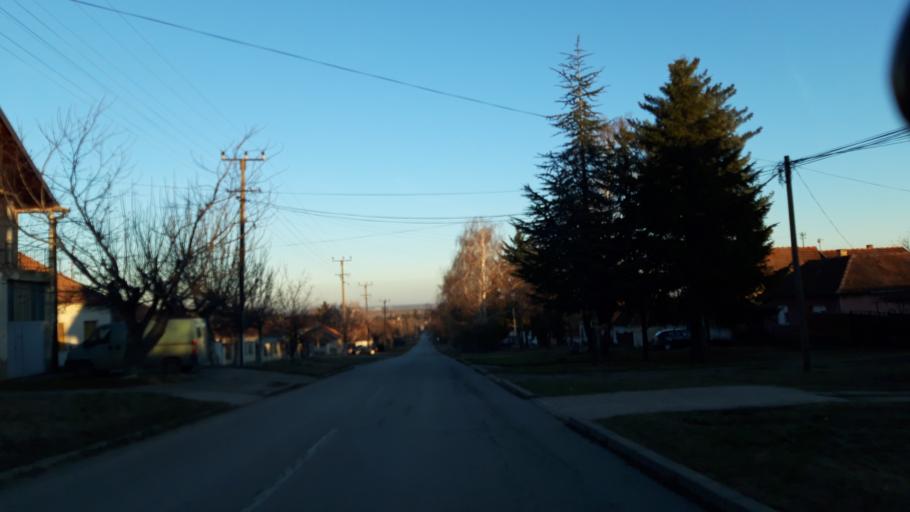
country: RS
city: Cortanovci
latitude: 45.1582
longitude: 20.0097
